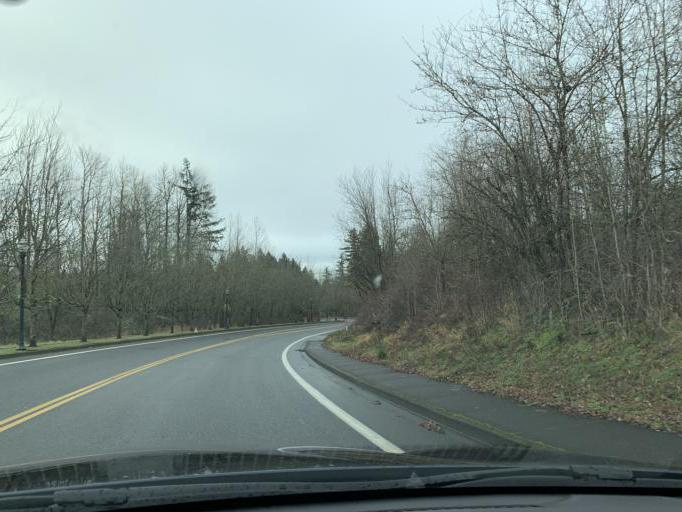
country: US
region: Washington
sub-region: Clark County
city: Camas
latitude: 45.5890
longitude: -122.4532
